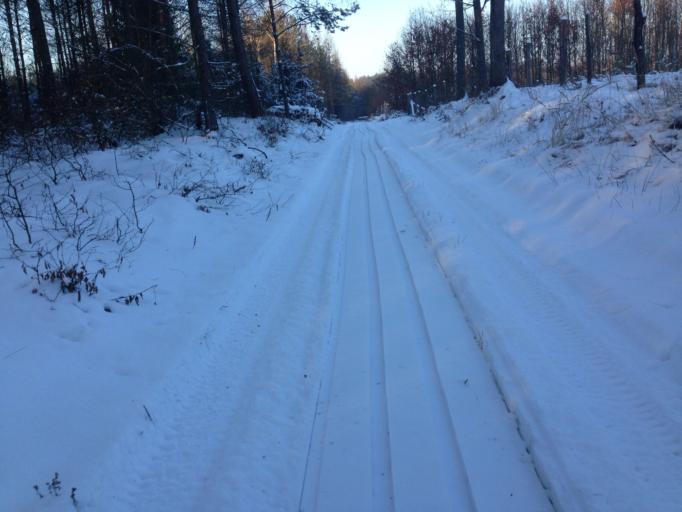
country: PL
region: Kujawsko-Pomorskie
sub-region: Powiat brodnicki
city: Gorzno
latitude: 53.1829
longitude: 19.6835
